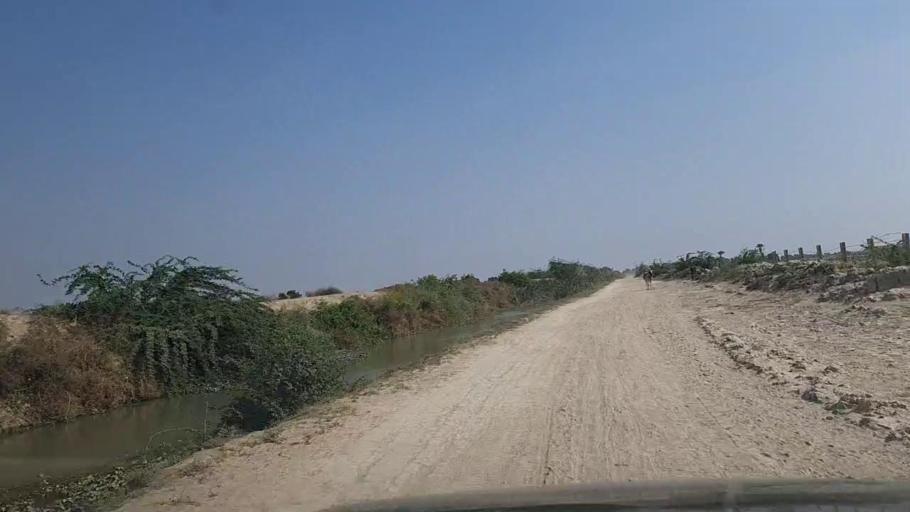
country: PK
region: Sindh
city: Gharo
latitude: 24.7134
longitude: 67.5837
